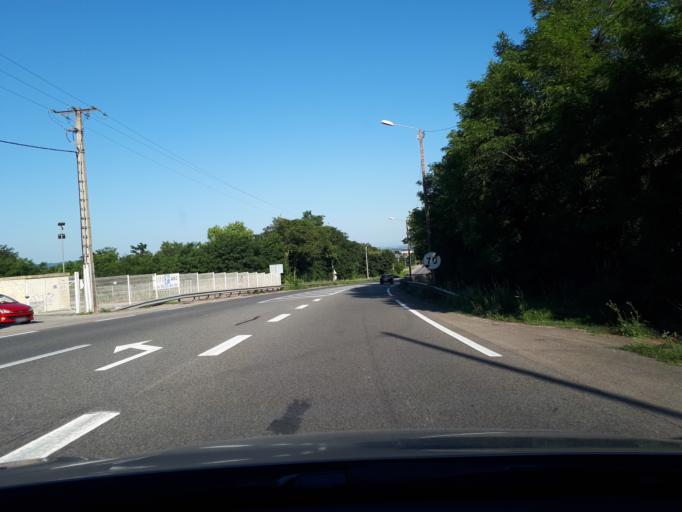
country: FR
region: Rhone-Alpes
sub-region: Departement de l'Isere
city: Grenay
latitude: 45.6668
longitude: 5.0895
